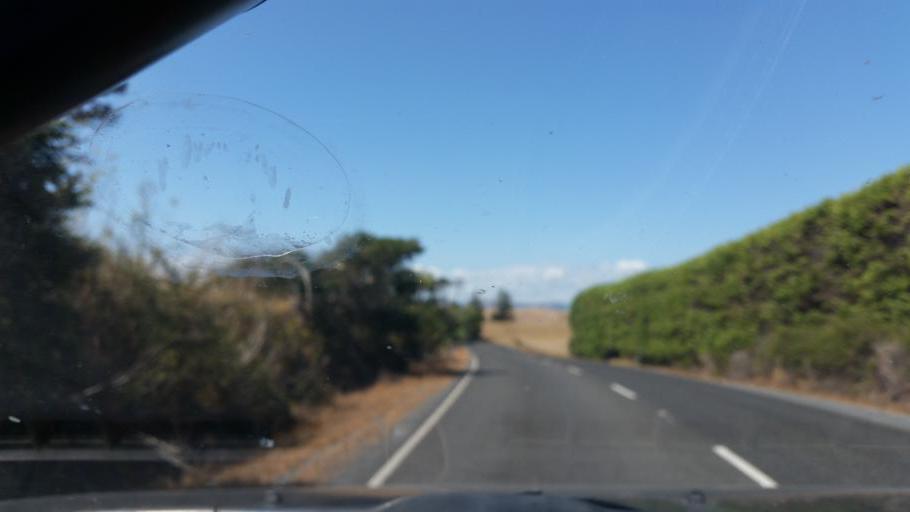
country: NZ
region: Northland
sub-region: Kaipara District
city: Dargaville
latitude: -35.9469
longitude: 173.7708
